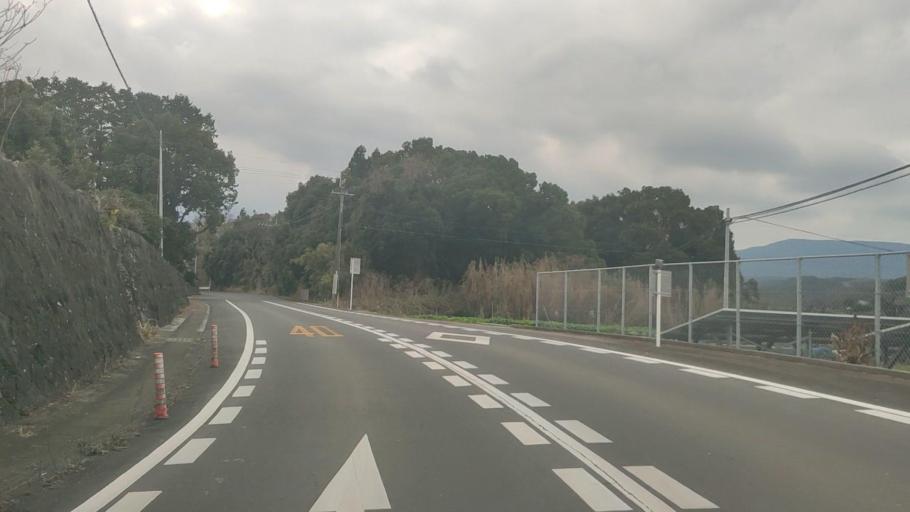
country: JP
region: Nagasaki
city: Shimabara
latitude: 32.8347
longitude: 130.2913
